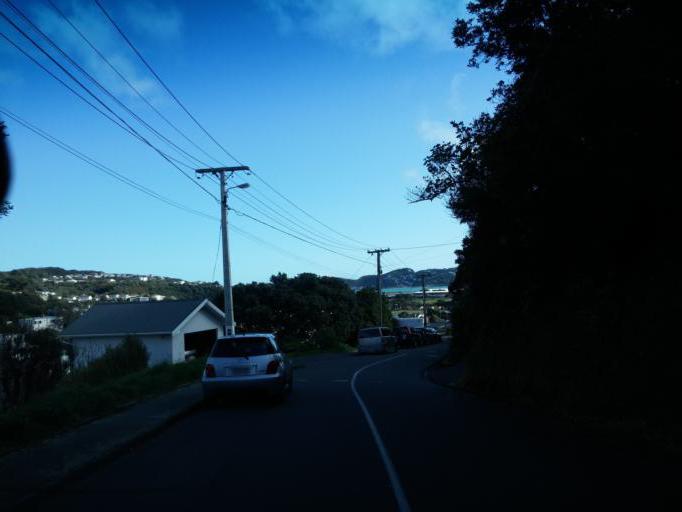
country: NZ
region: Wellington
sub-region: Wellington City
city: Wellington
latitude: -41.3235
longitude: 174.8263
